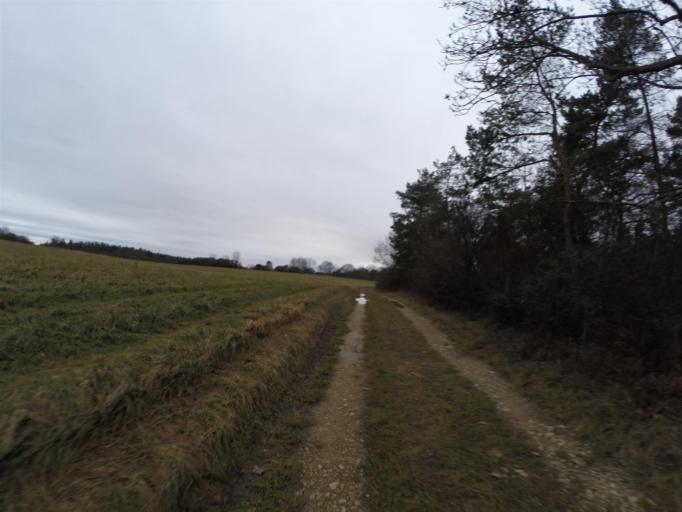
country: DE
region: Thuringia
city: Jena
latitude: 50.9143
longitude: 11.6161
